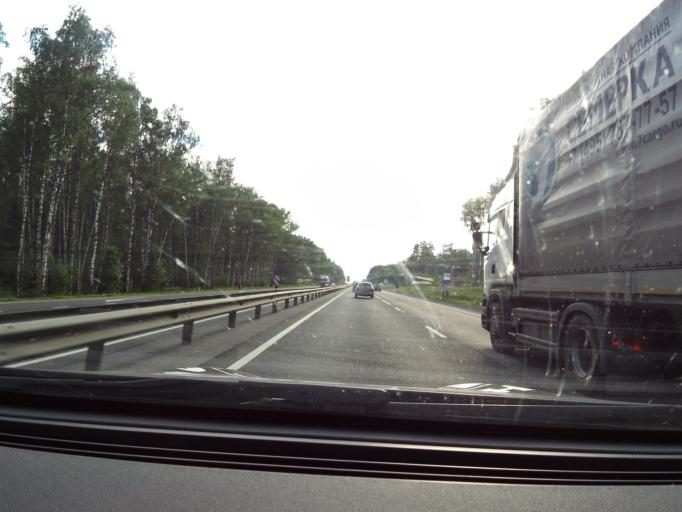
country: RU
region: Vladimir
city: Kameshkovo
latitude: 56.1965
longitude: 40.9949
